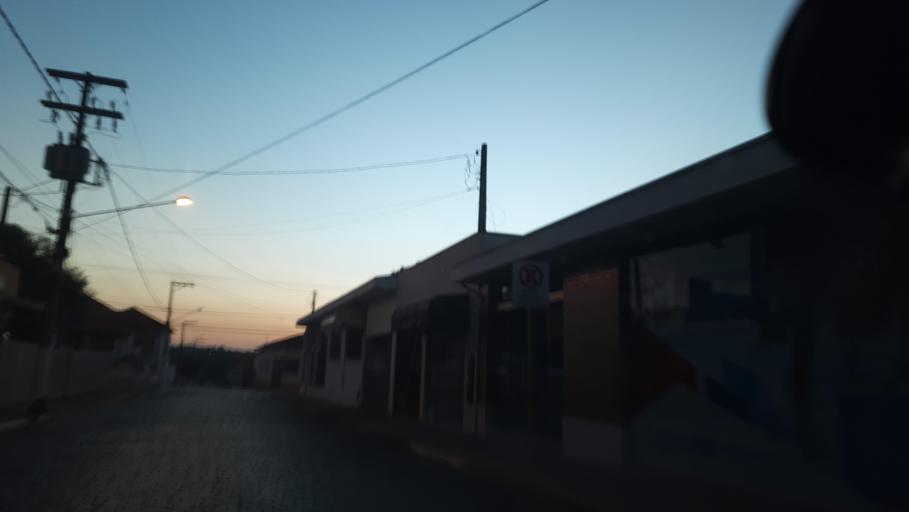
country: BR
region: Sao Paulo
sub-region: Casa Branca
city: Casa Branca
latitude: -21.7750
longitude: -47.0856
